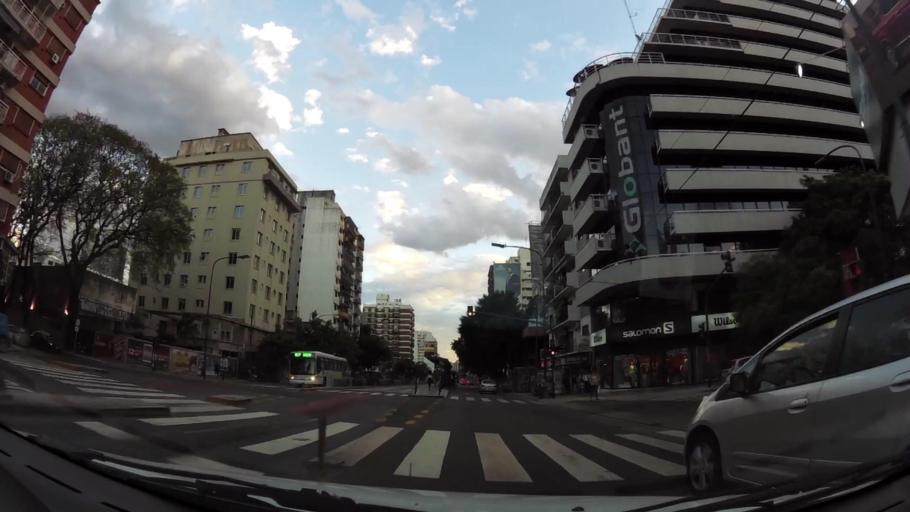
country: AR
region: Buenos Aires F.D.
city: Colegiales
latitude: -34.5438
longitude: -58.4723
